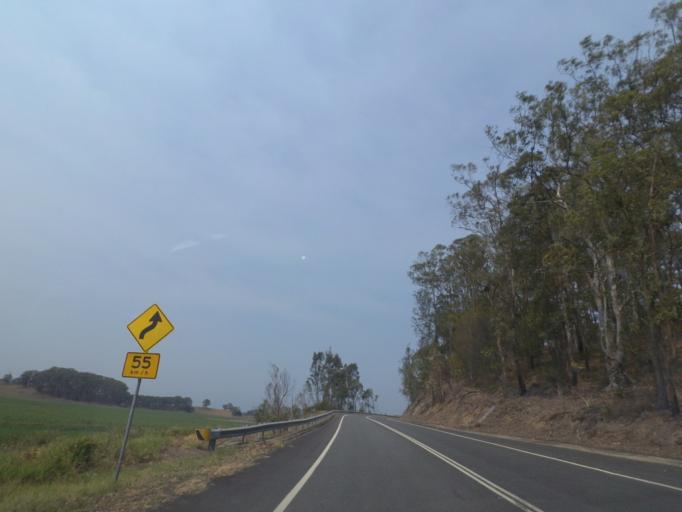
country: AU
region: New South Wales
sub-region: Tweed
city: Burringbar
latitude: -28.4582
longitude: 153.5206
